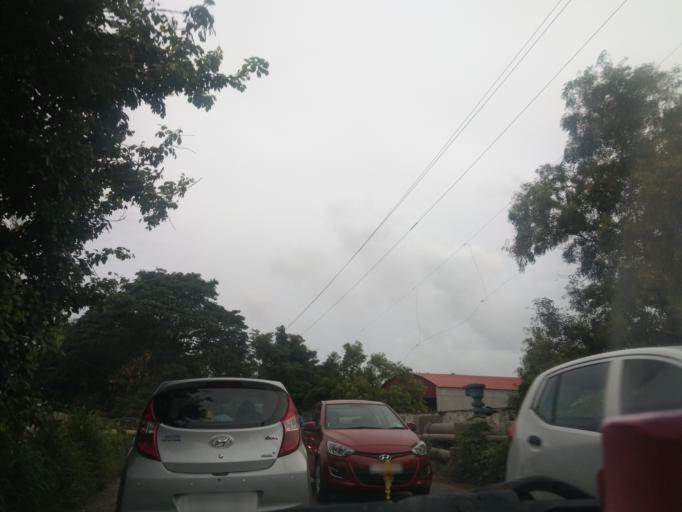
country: IN
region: Goa
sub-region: South Goa
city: Davorlim
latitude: 15.2680
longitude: 73.9777
